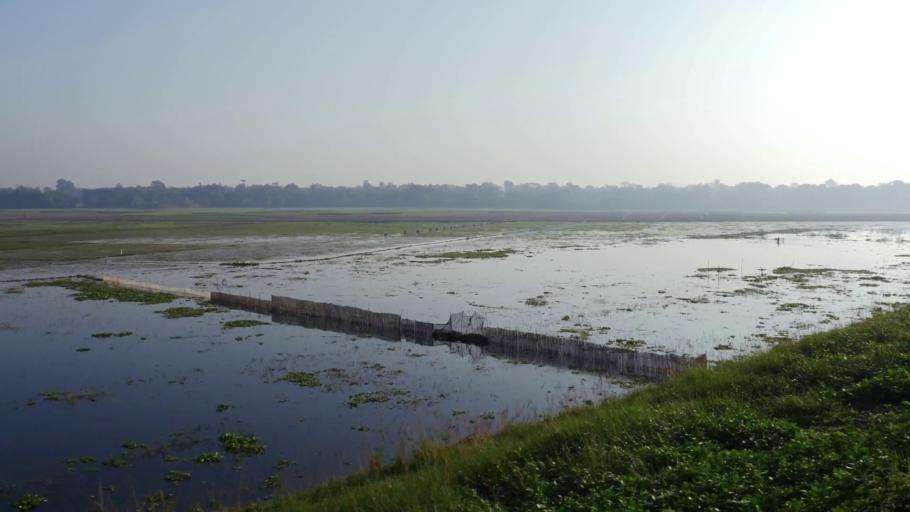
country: BD
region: Dhaka
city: Jamalpur
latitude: 24.9183
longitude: 89.9446
